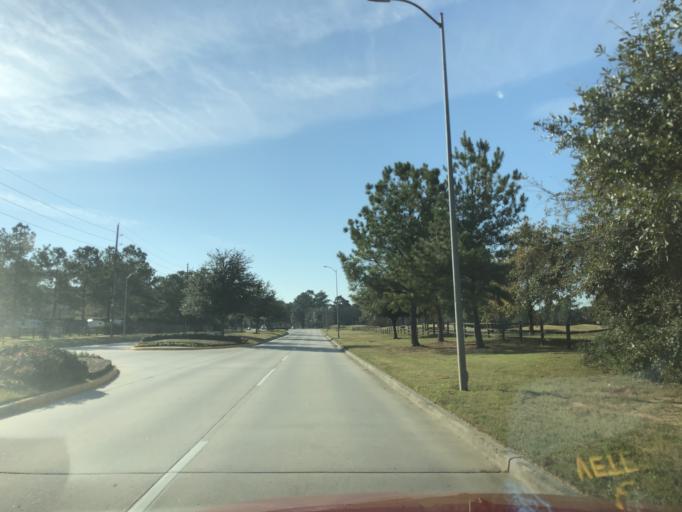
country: US
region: Texas
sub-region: Harris County
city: Tomball
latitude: 30.0415
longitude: -95.5632
